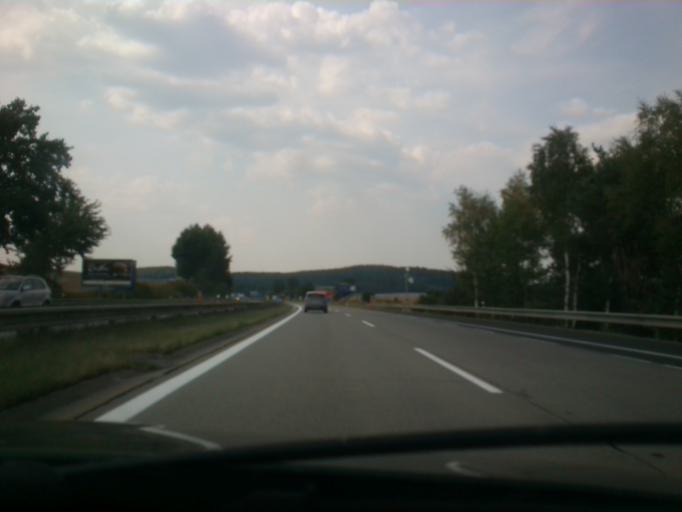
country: CZ
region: Central Bohemia
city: Divisov
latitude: 49.8284
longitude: 14.8646
